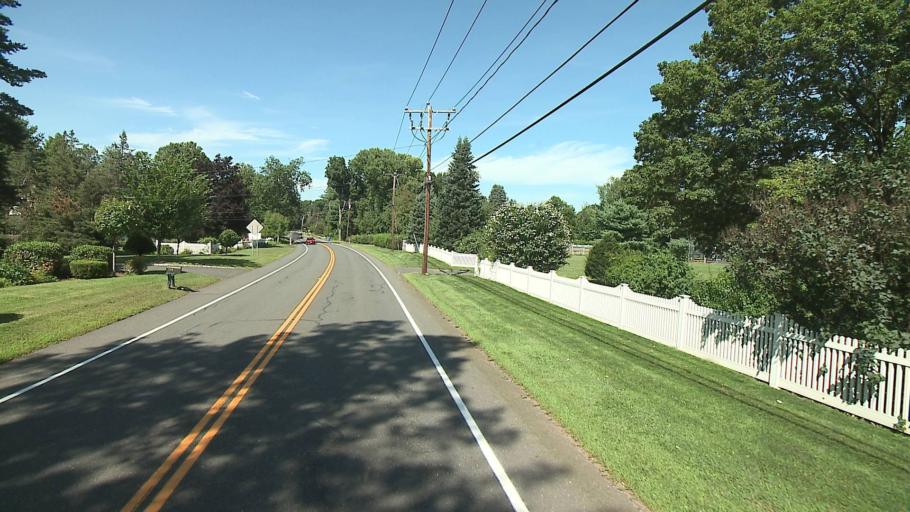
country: US
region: Connecticut
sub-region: Hartford County
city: Weatogue
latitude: 41.8513
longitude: -72.8344
